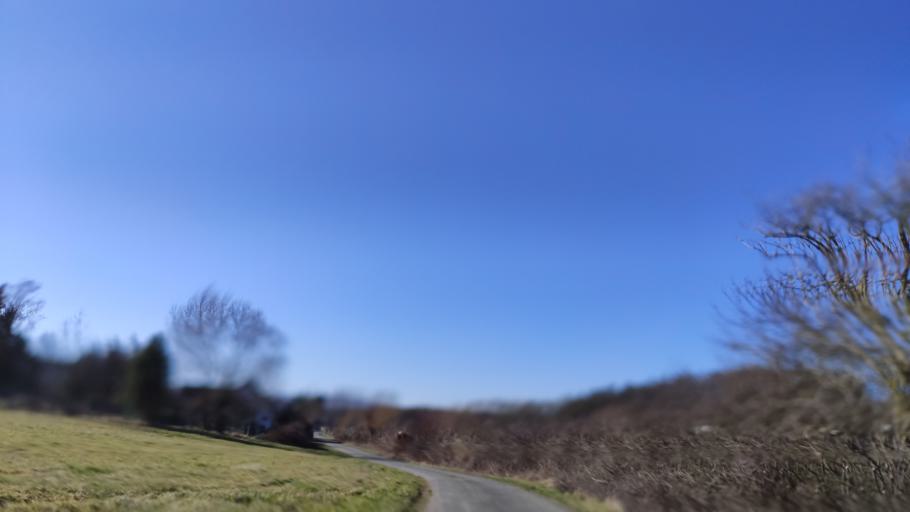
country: DE
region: North Rhine-Westphalia
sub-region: Regierungsbezirk Detmold
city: Steinheim
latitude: 51.8791
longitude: 9.1087
